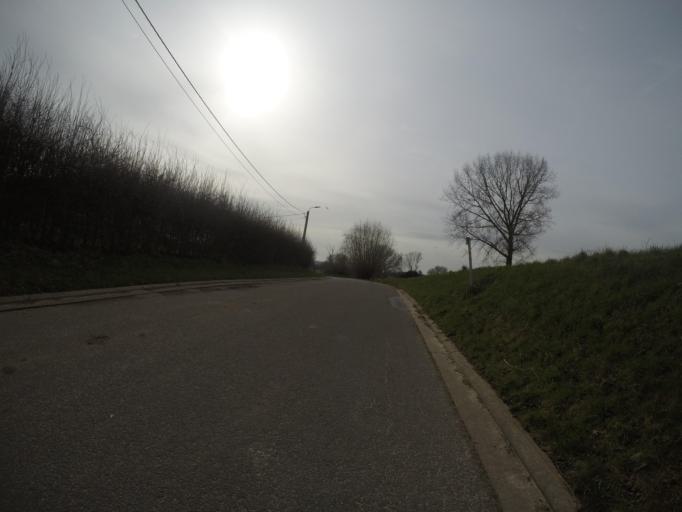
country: BE
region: Flanders
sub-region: Provincie Oost-Vlaanderen
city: Sint-Maria-Lierde
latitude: 50.8339
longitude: 3.8443
